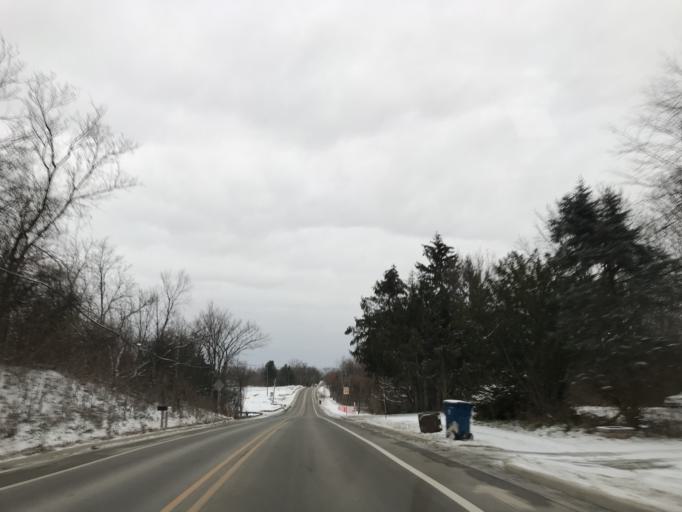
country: US
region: Michigan
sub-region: Washtenaw County
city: Ann Arbor
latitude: 42.3095
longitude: -83.7349
